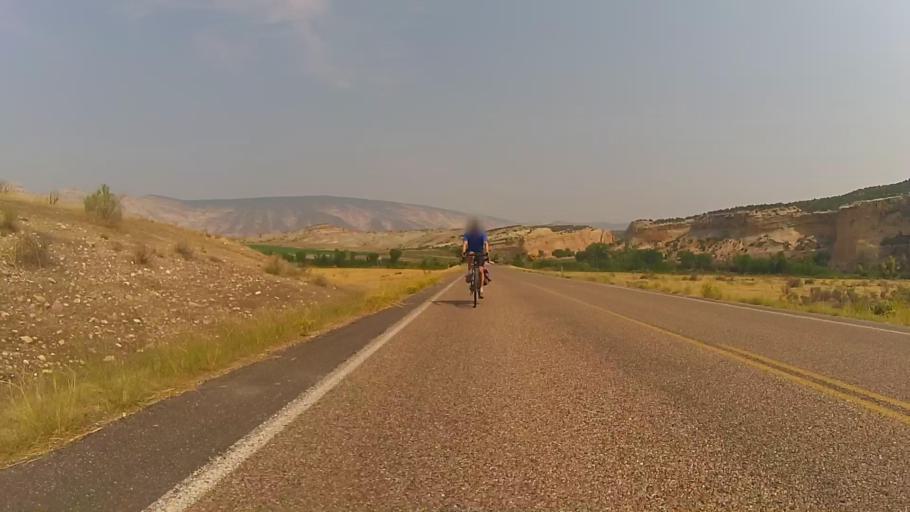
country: US
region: Utah
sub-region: Uintah County
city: Naples
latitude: 40.4081
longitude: -109.2371
